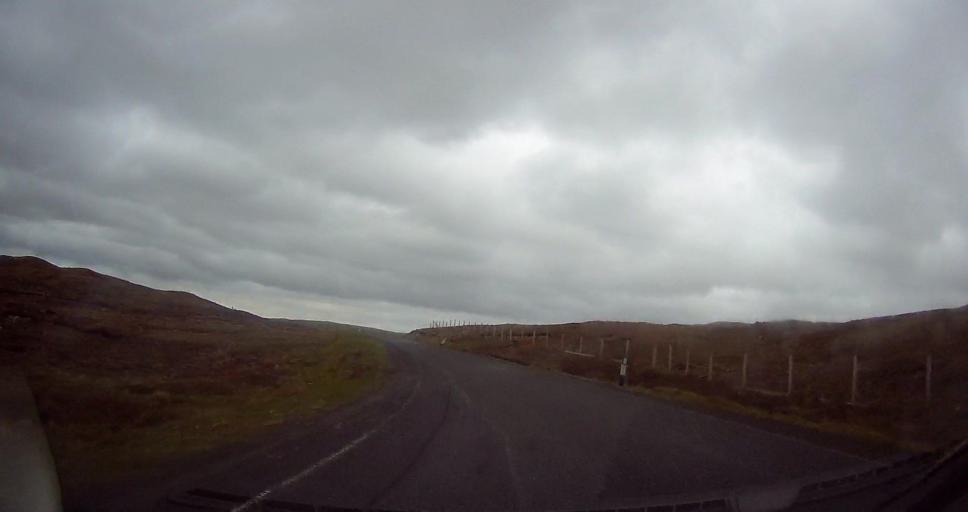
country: GB
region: Scotland
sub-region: Shetland Islands
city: Lerwick
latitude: 60.4799
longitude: -1.4182
